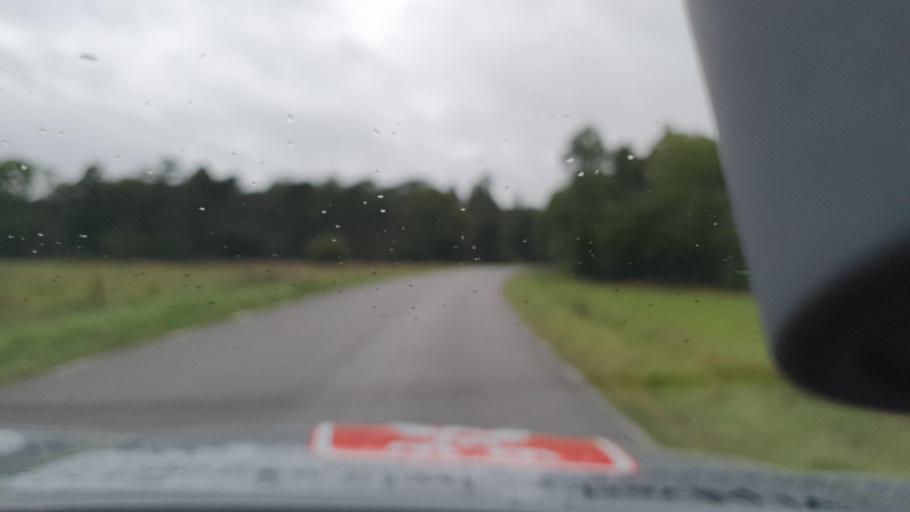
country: SE
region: Gotland
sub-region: Gotland
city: Visby
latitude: 57.7766
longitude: 18.4978
